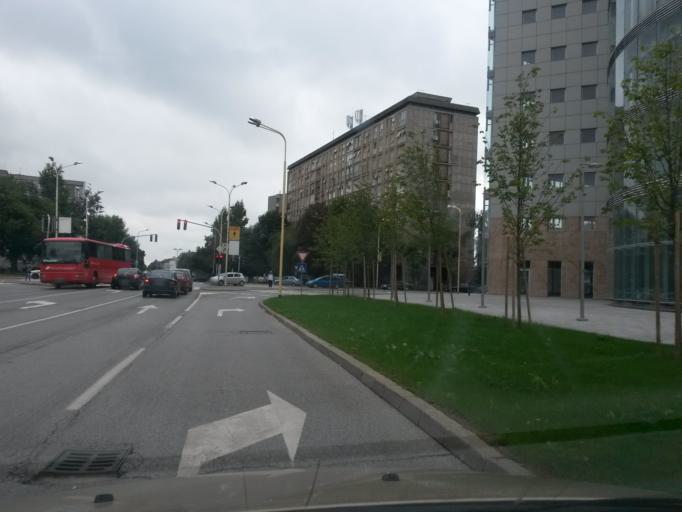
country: HR
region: Osjecko-Baranjska
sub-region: Grad Osijek
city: Osijek
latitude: 45.5554
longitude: 18.6956
